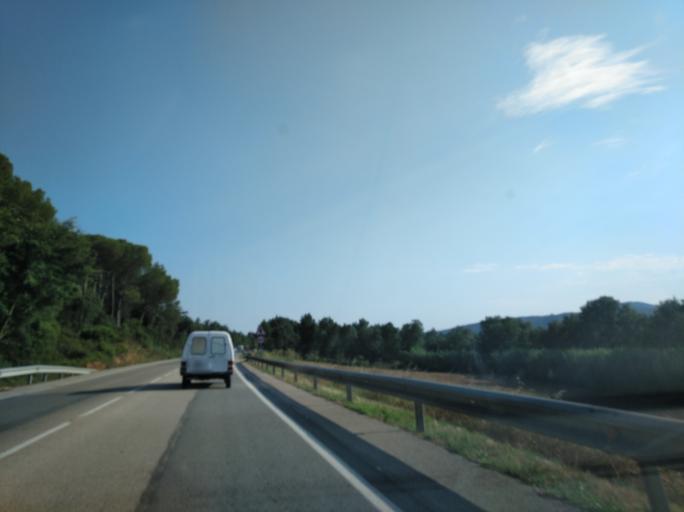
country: ES
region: Catalonia
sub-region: Provincia de Girona
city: Santa Coloma de Farners
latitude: 41.8723
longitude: 2.6914
